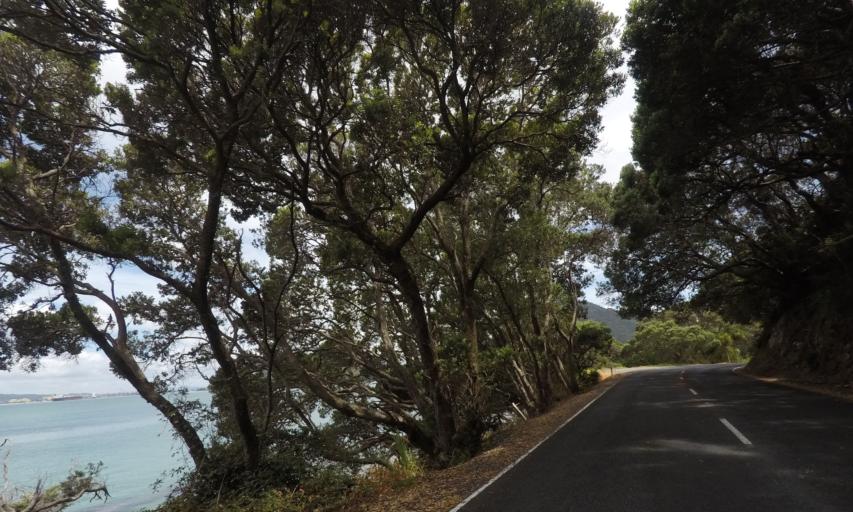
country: NZ
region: Northland
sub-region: Whangarei
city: Ruakaka
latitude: -35.8374
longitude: 174.5335
